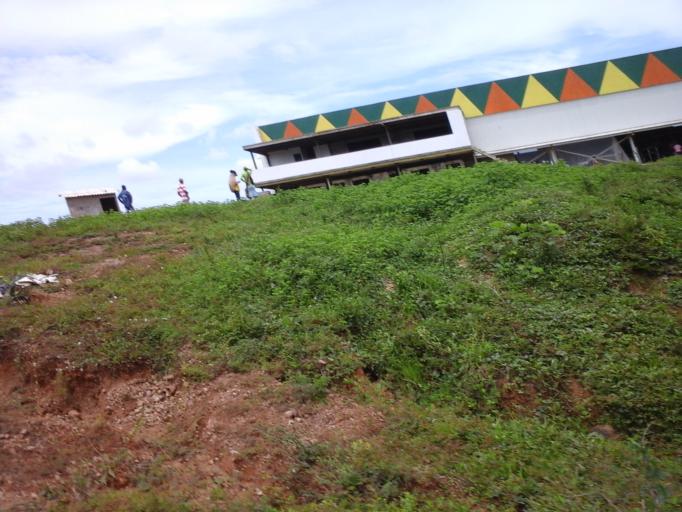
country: CO
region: Bolivar
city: San Cristobal
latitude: 9.8837
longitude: -75.3031
